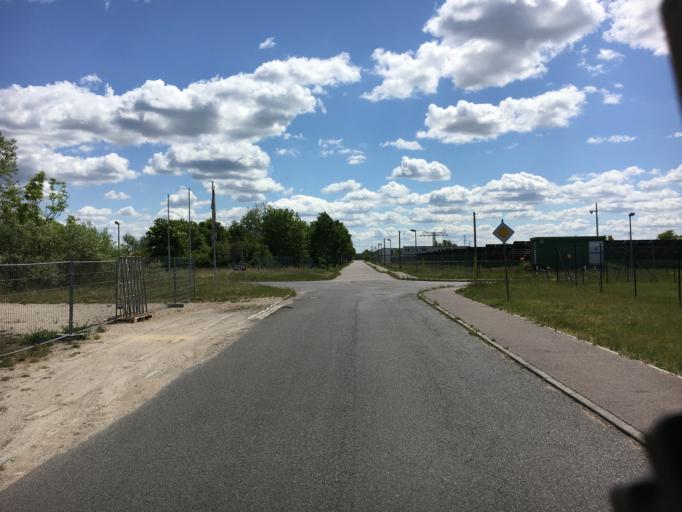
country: DE
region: Brandenburg
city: Trebbin
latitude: 52.1892
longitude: 13.2380
